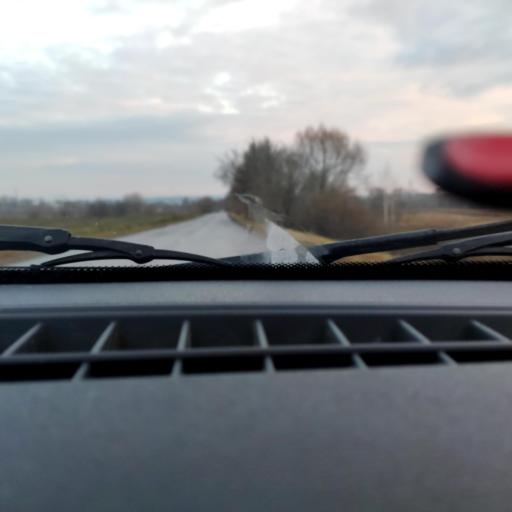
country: RU
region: Bashkortostan
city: Avdon
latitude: 54.5065
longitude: 55.8774
